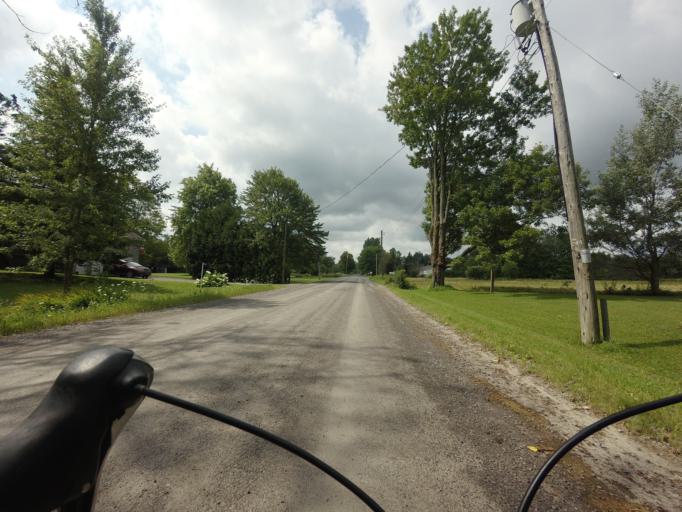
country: CA
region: Ontario
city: Brockville
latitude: 44.7109
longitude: -75.6989
